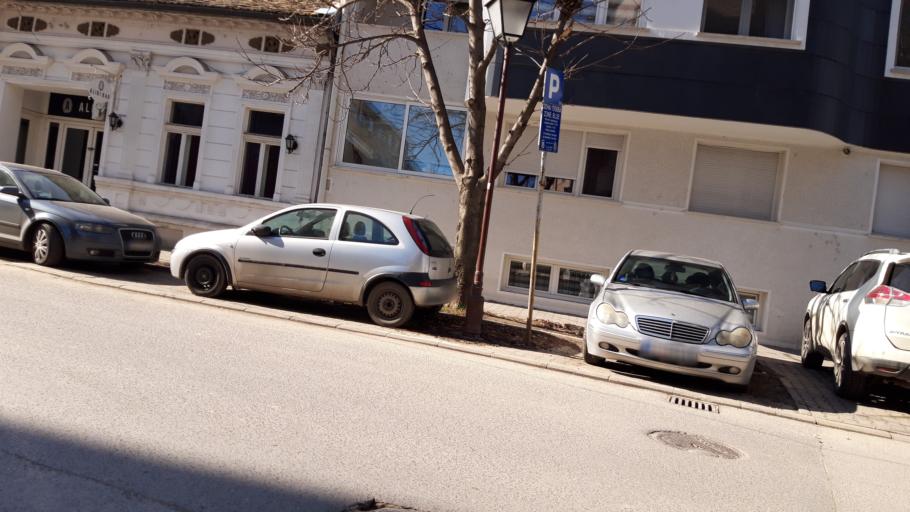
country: RS
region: Autonomna Pokrajina Vojvodina
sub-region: Juznobacki Okrug
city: Novi Sad
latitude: 45.2578
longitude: 19.8382
